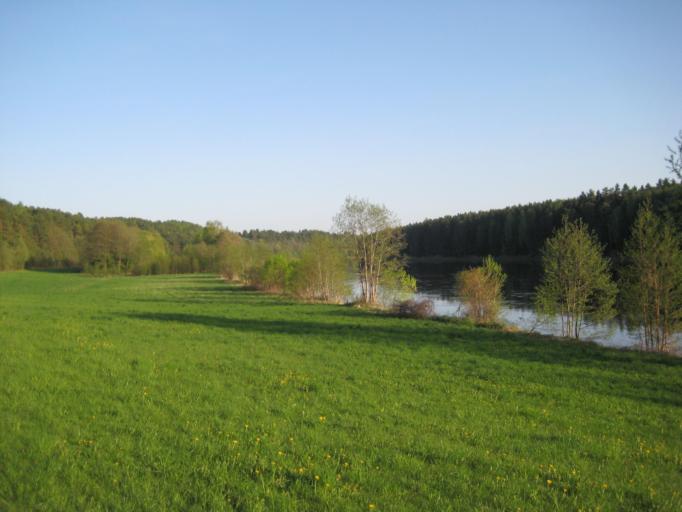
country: LT
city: Birstonas
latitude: 54.6041
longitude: 24.0079
